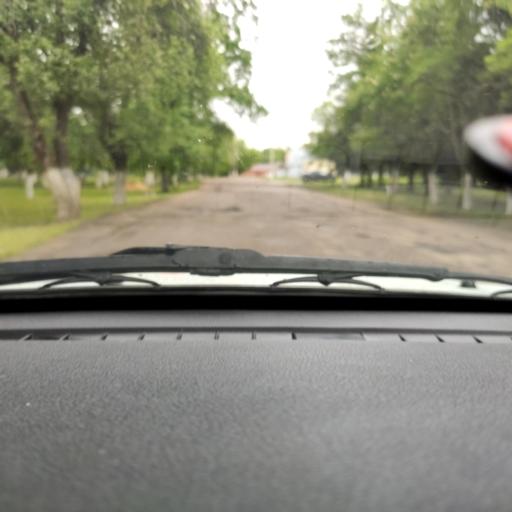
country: RU
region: Voronezj
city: Devitsa
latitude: 51.6043
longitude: 38.9999
